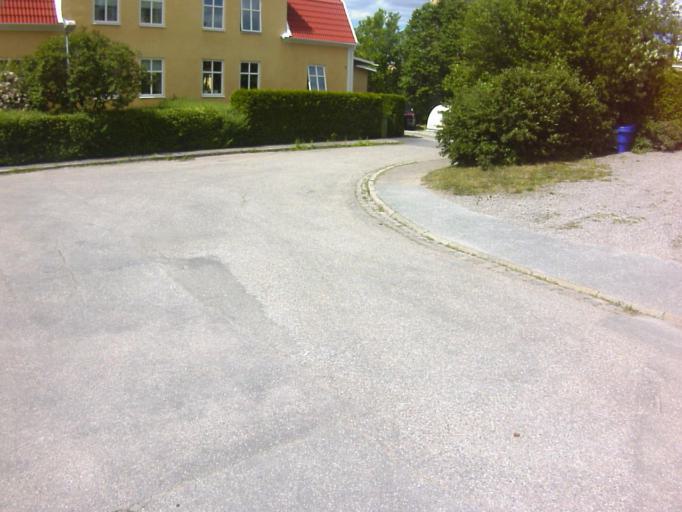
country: SE
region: Soedermanland
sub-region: Eskilstuna Kommun
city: Eskilstuna
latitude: 59.3675
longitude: 16.5002
